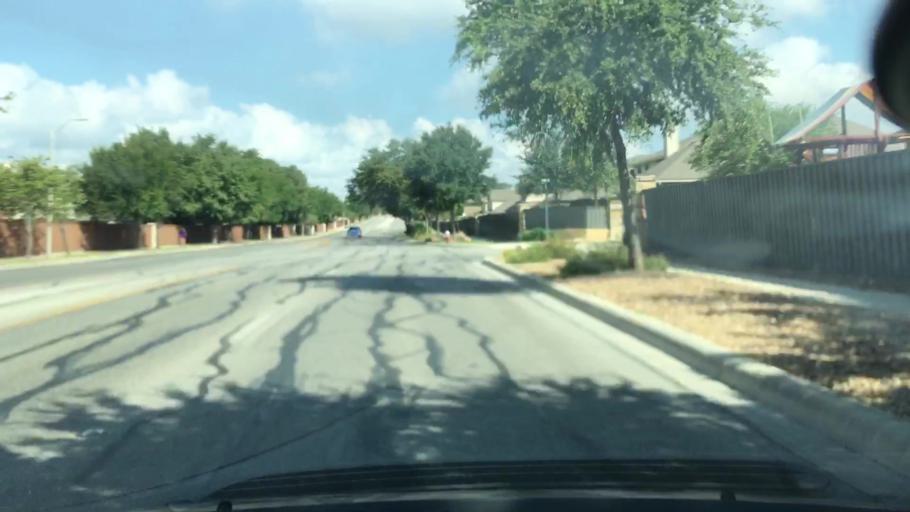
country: US
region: Texas
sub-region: Guadalupe County
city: Cibolo
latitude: 29.5765
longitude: -98.2435
